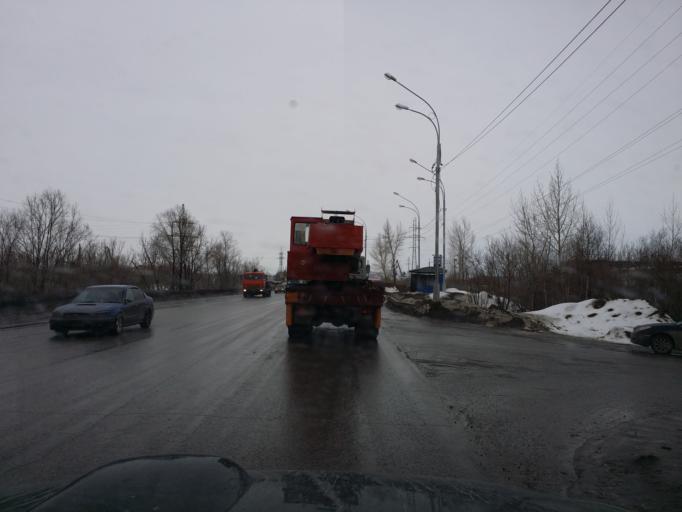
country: RU
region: Khanty-Mansiyskiy Avtonomnyy Okrug
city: Nizhnevartovsk
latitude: 60.9321
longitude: 76.5311
